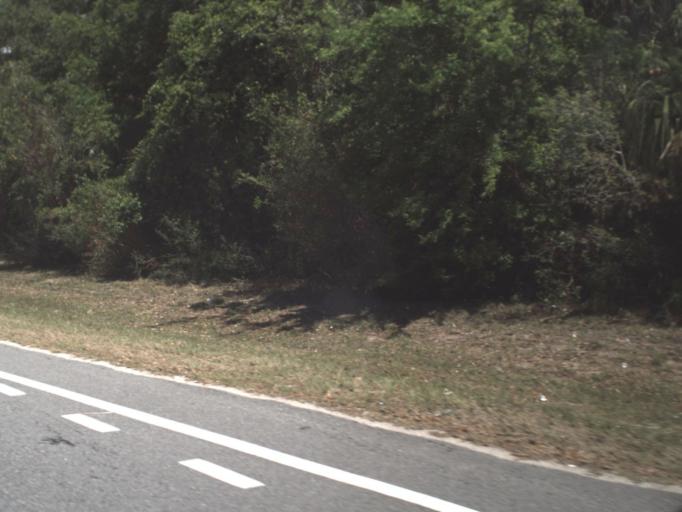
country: US
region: Florida
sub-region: Flagler County
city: Palm Coast
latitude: 29.6026
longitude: -81.1978
